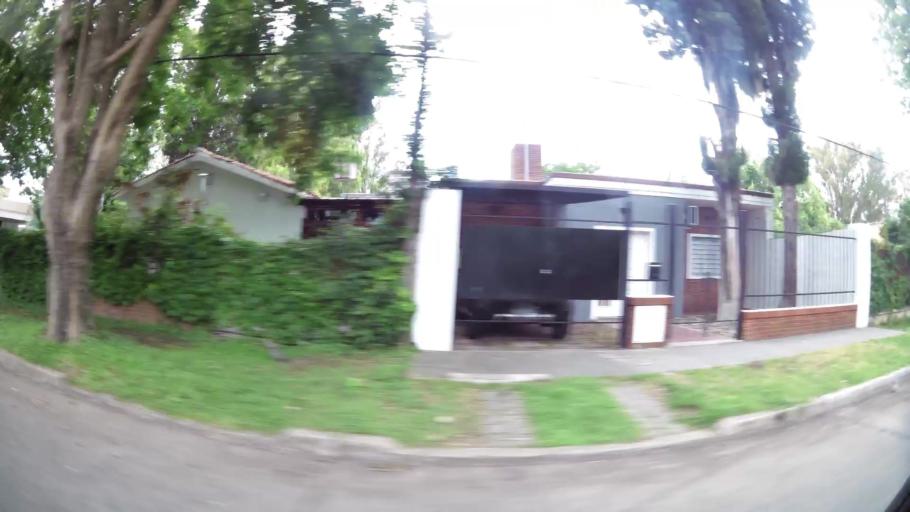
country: AR
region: Santa Fe
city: Granadero Baigorria
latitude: -32.8776
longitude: -60.6887
